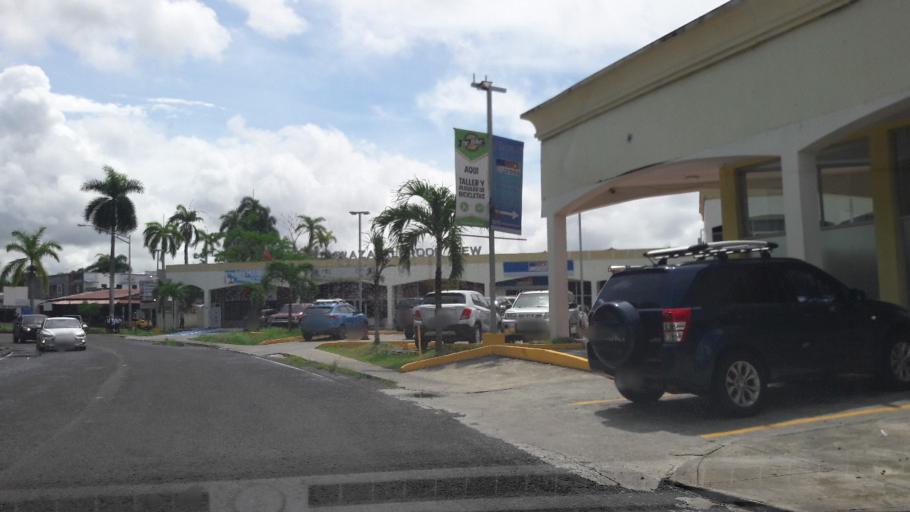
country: PA
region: Panama
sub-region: Distrito de Panama
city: Ancon
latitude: 8.9726
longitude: -79.5632
